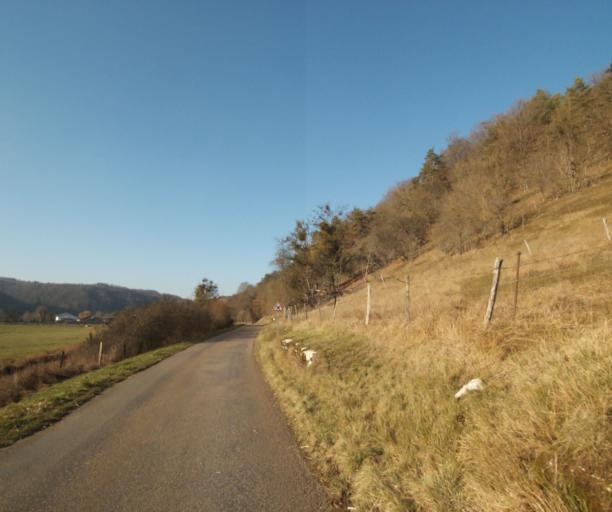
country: FR
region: Champagne-Ardenne
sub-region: Departement de la Haute-Marne
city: Joinville
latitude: 48.4900
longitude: 5.2000
